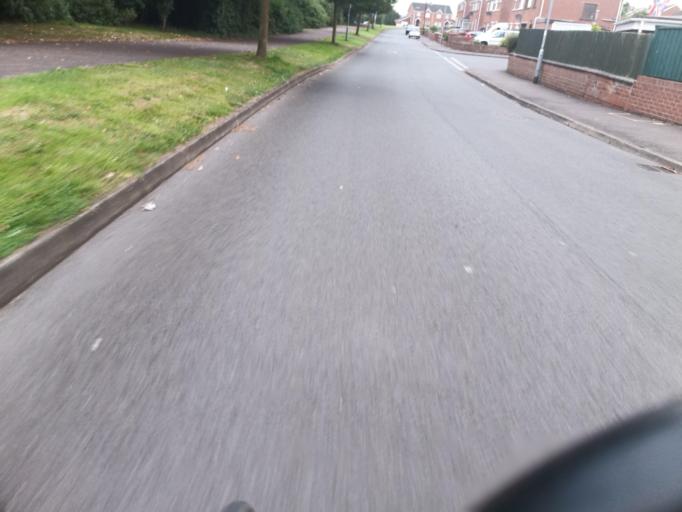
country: GB
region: Northern Ireland
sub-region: Ards District
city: Comber
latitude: 54.5525
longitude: -5.7319
